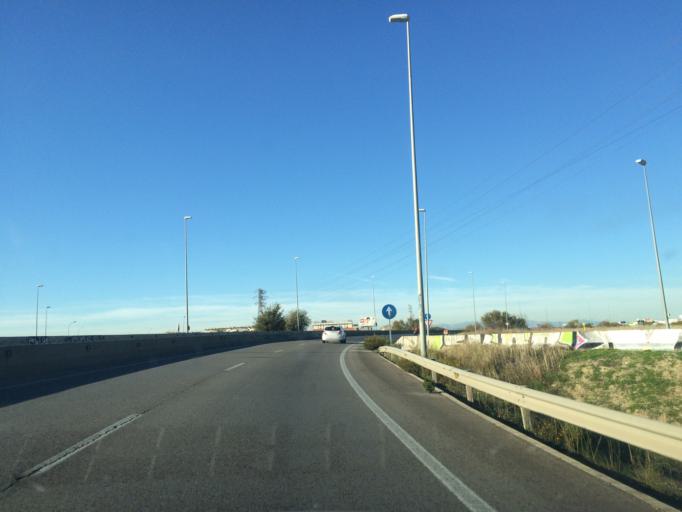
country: ES
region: Madrid
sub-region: Provincia de Madrid
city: Mostoles
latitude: 40.3312
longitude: -3.8523
